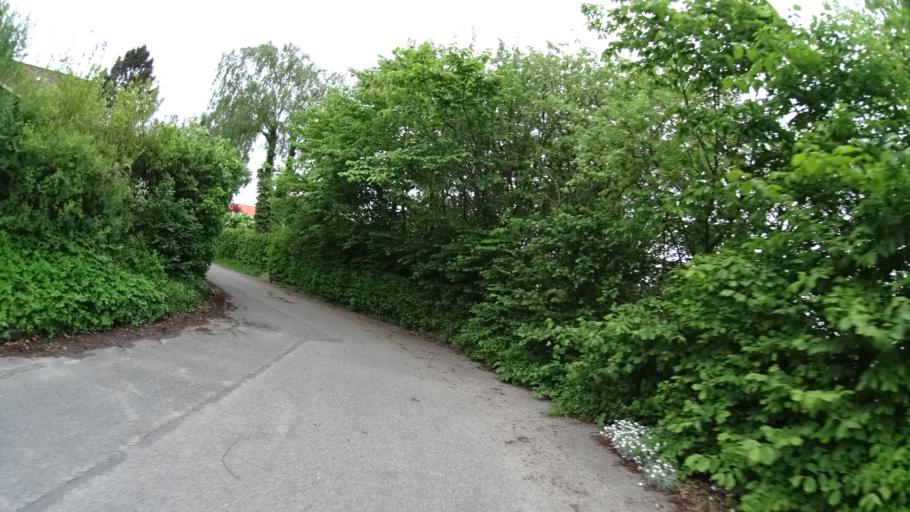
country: DK
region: Central Jutland
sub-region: Arhus Kommune
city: Arhus
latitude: 56.1343
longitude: 10.1720
